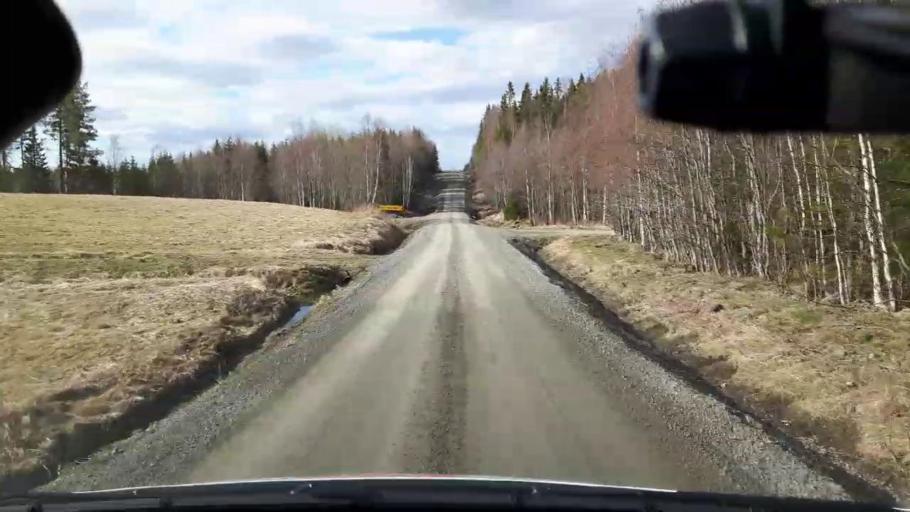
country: SE
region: Jaemtland
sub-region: Bergs Kommun
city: Hoverberg
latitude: 62.8542
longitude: 14.6693
